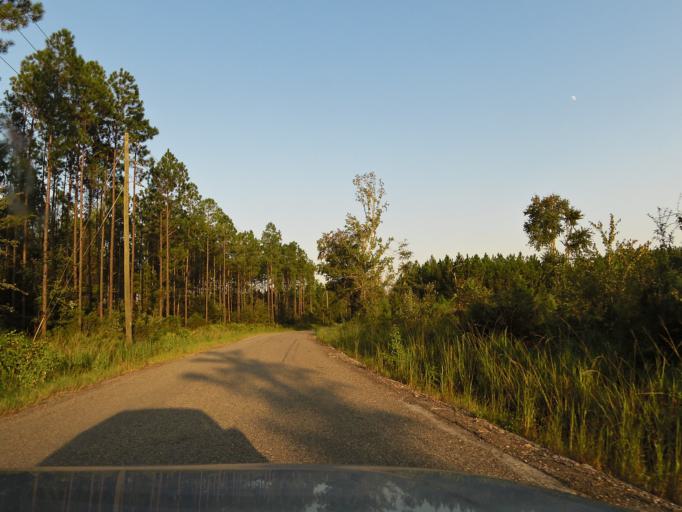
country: US
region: Florida
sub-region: Duval County
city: Baldwin
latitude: 30.3882
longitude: -82.0506
